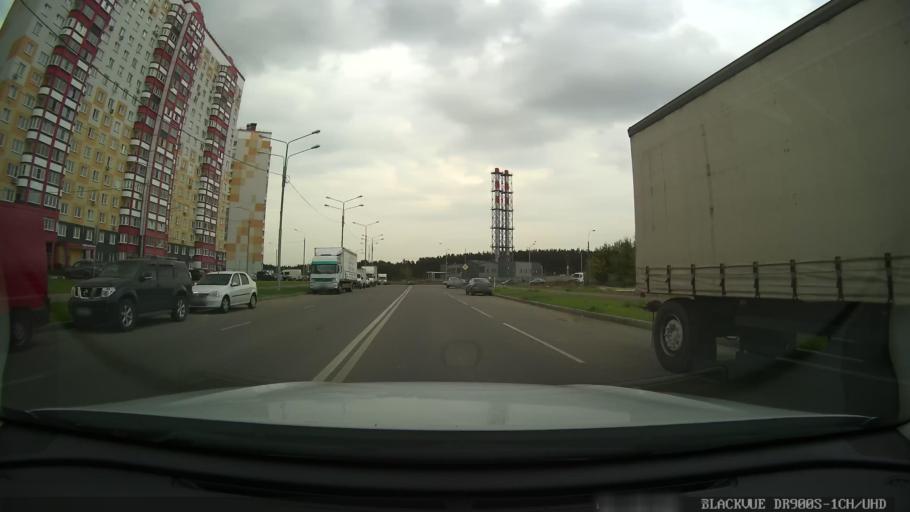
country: RU
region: Moskovskaya
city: Shcherbinka
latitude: 55.5203
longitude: 37.5848
